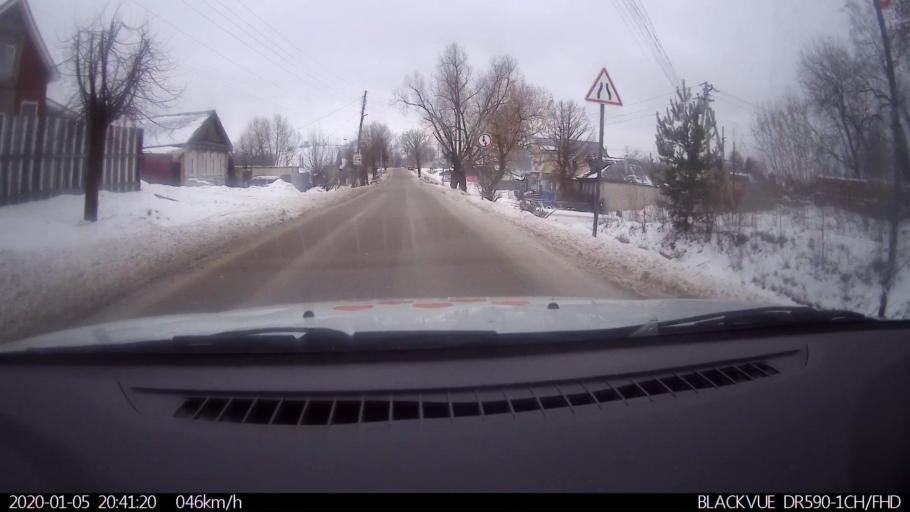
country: RU
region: Nizjnij Novgorod
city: Lukino
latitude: 56.4042
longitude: 43.7289
